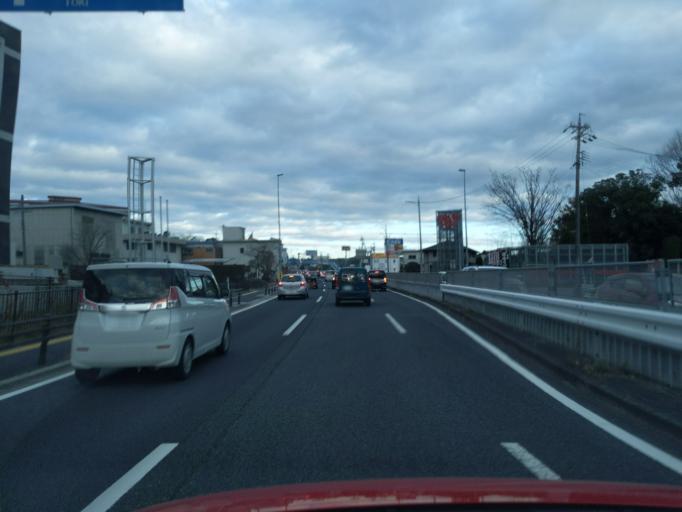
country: JP
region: Gifu
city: Tajimi
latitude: 35.3407
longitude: 137.1306
